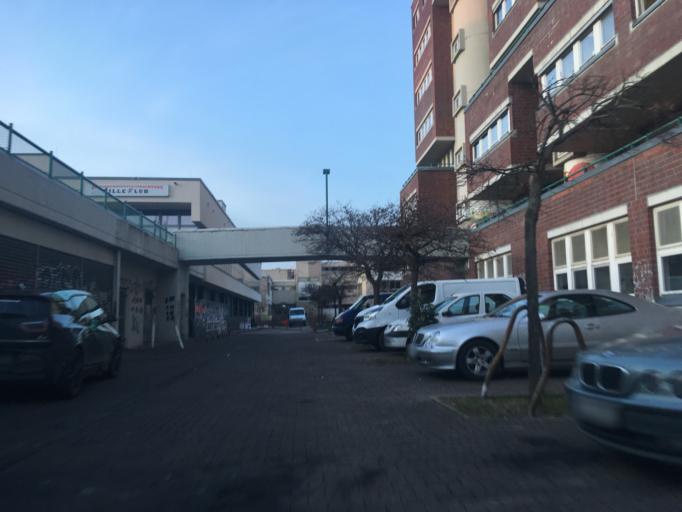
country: DE
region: Berlin
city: Moabit
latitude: 52.5294
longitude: 13.3539
